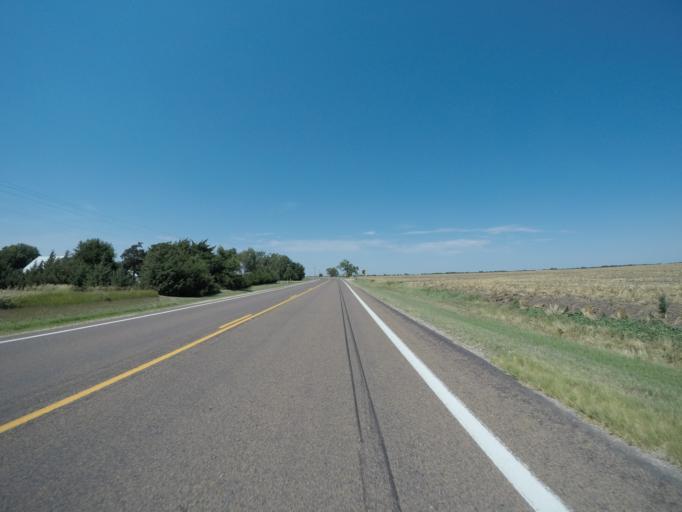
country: US
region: Kansas
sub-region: Mitchell County
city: Beloit
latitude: 39.5622
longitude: -98.1151
